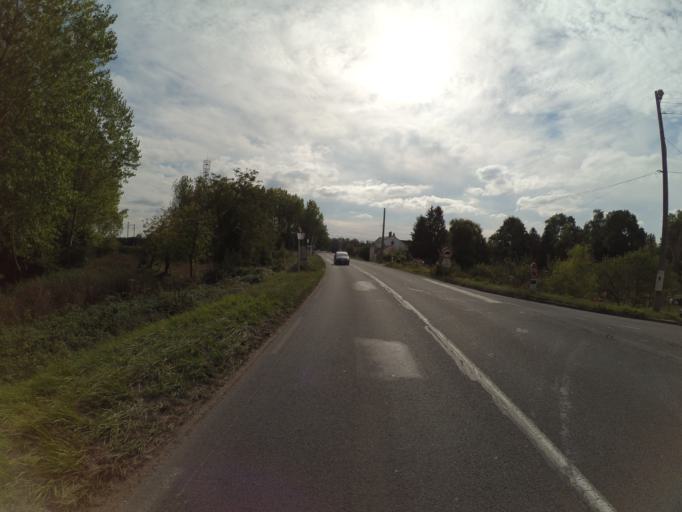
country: FR
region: Centre
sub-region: Departement d'Indre-et-Loire
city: Langeais
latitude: 47.3090
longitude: 0.3630
